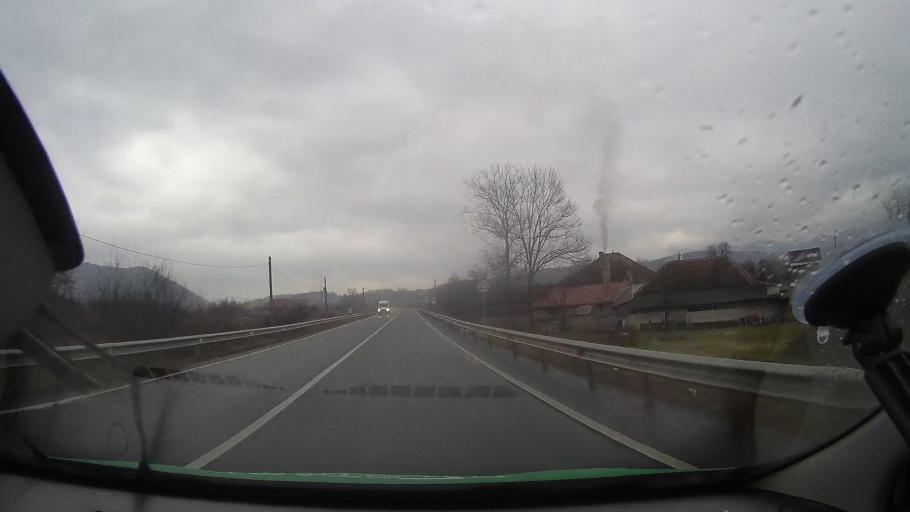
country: RO
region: Hunedoara
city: Vata de Jos
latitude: 46.1885
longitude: 22.6223
